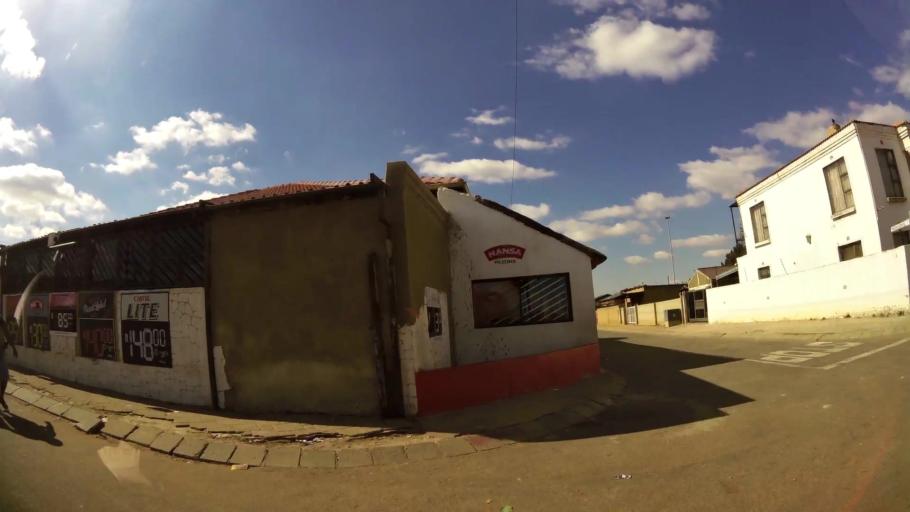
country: ZA
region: Gauteng
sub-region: West Rand District Municipality
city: Krugersdorp
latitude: -26.1425
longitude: 27.7963
